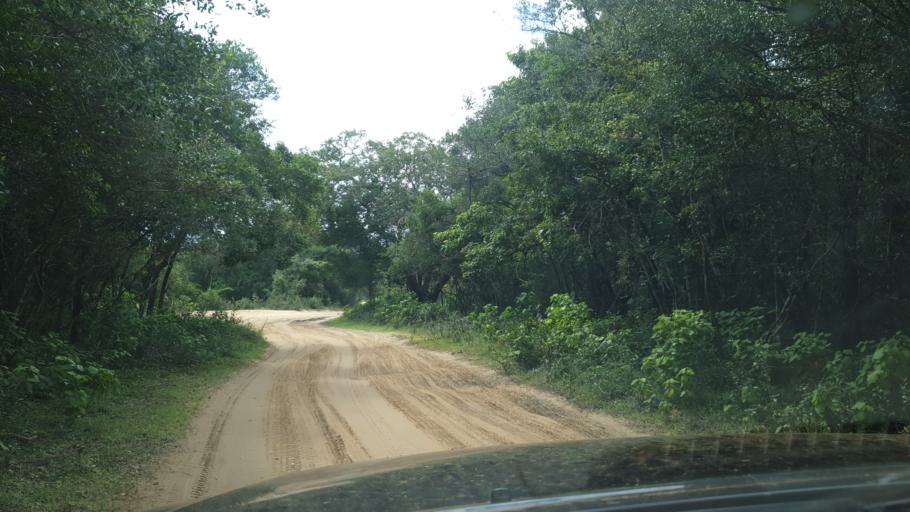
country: LK
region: North Western
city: Puttalam
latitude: 8.4160
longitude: 79.9992
